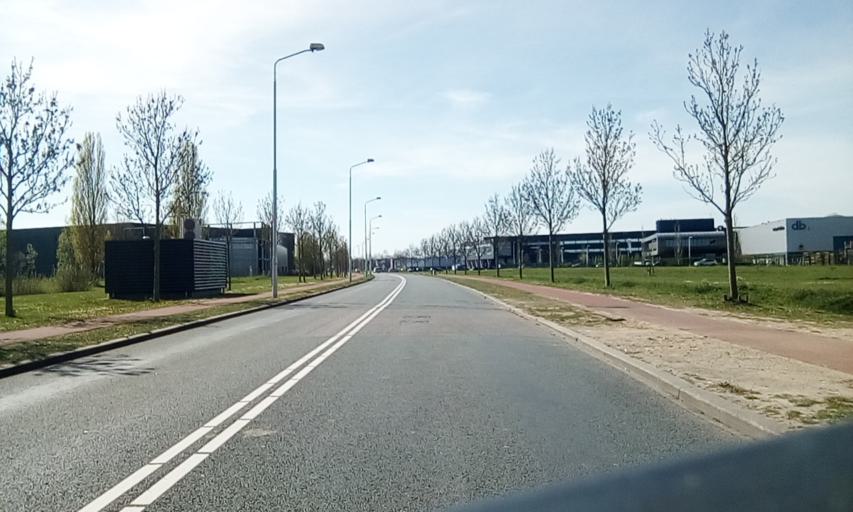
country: NL
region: Gelderland
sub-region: Gemeente Beuningen
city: Beuningen
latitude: 51.8306
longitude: 5.7527
